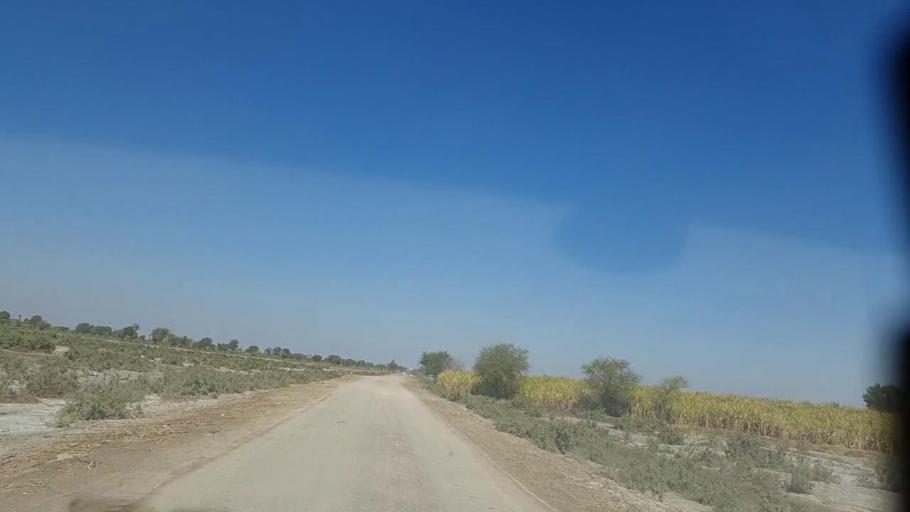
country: PK
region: Sindh
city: Digri
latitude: 25.1710
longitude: 69.0486
